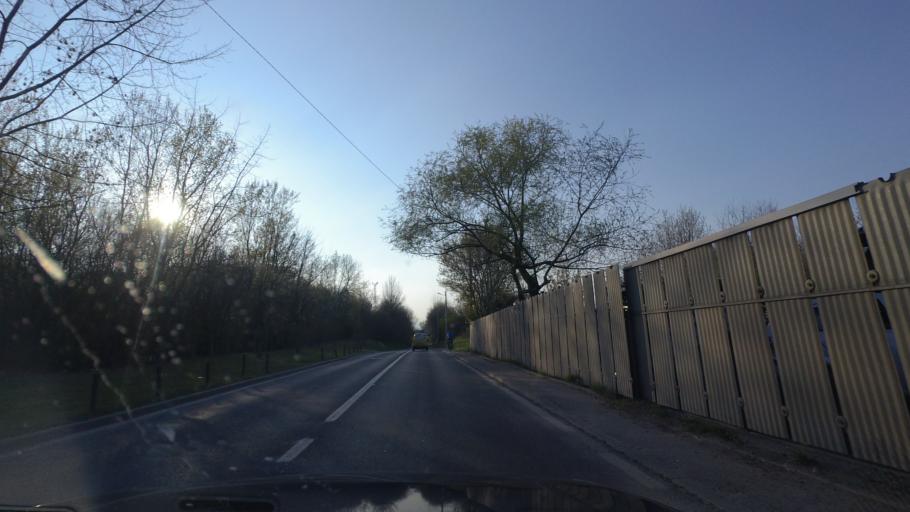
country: HR
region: Grad Zagreb
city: Dubrava
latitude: 45.8071
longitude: 16.0688
